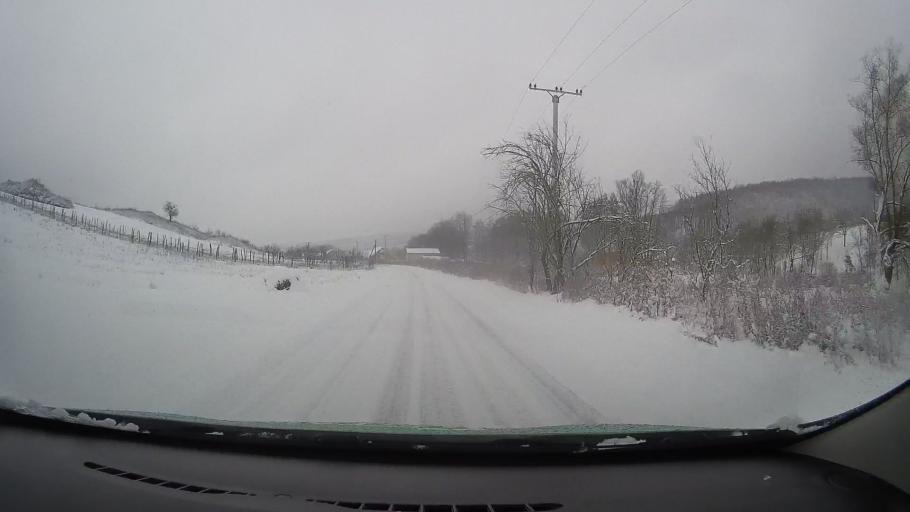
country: RO
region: Hunedoara
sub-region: Comuna Carjiti
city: Carjiti
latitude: 45.8320
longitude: 22.8416
